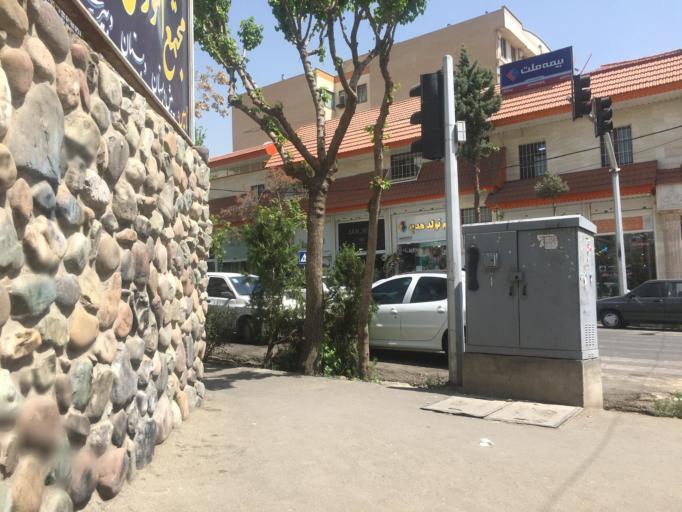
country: IR
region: Tehran
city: Tehran
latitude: 35.7430
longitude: 51.5487
